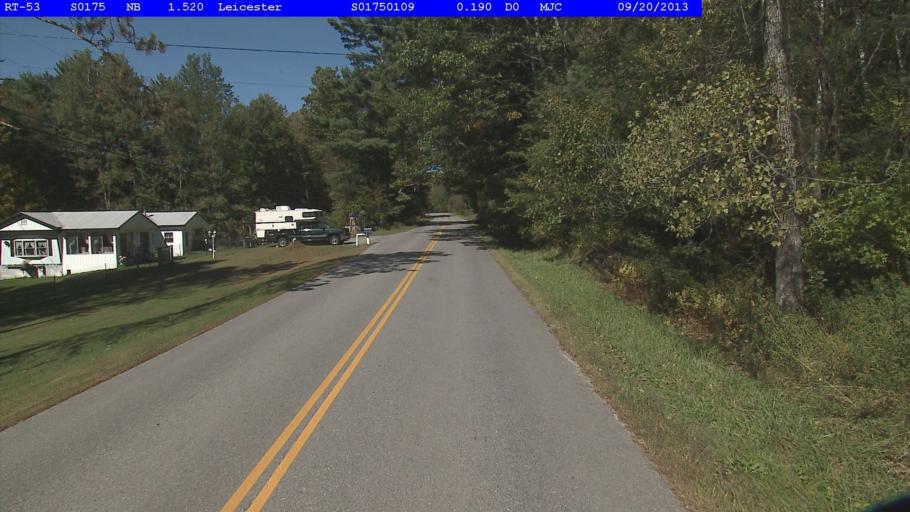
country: US
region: Vermont
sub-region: Rutland County
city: Brandon
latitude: 43.8486
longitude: -73.0582
